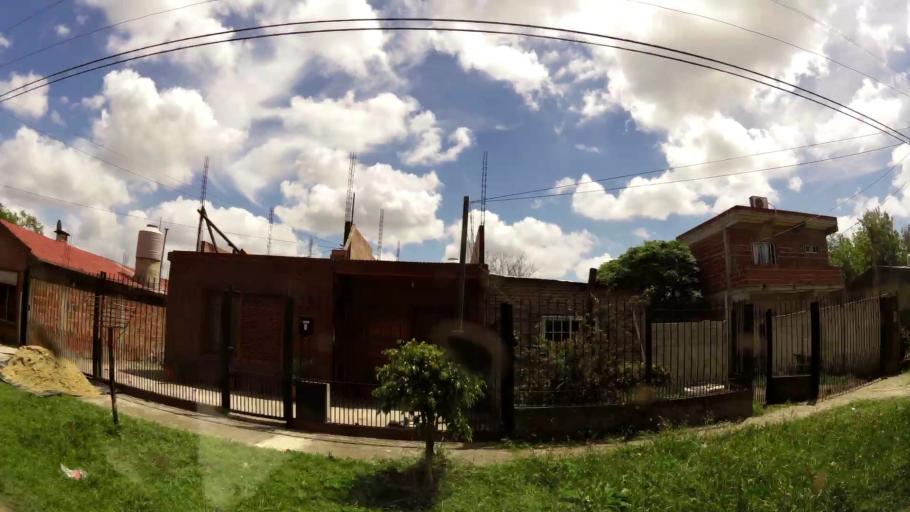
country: AR
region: Buenos Aires
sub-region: Partido de Quilmes
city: Quilmes
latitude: -34.8227
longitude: -58.2347
